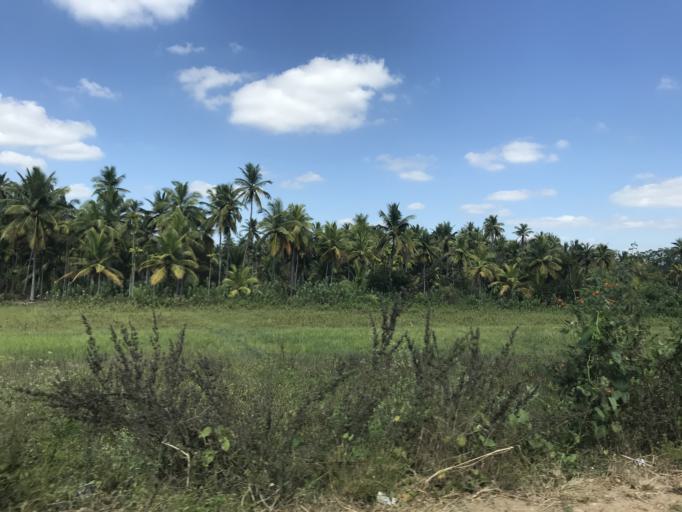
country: IN
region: Karnataka
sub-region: Mandya
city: Krishnarajpet
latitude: 12.5925
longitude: 76.3574
